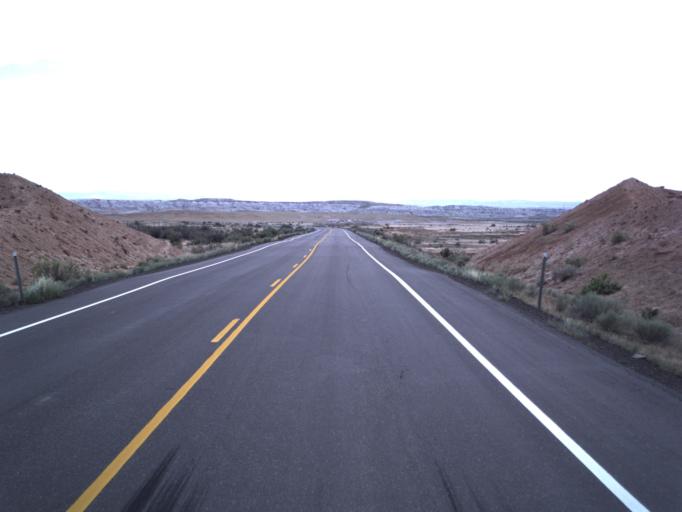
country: US
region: Utah
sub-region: Uintah County
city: Naples
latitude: 40.1251
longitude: -109.2596
